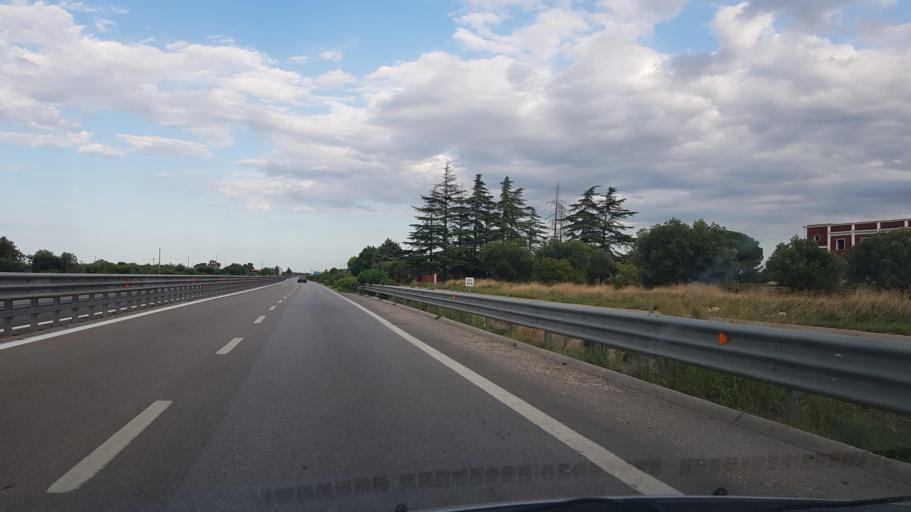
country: IT
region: Apulia
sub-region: Provincia di Taranto
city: Grottaglie
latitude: 40.5342
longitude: 17.4691
